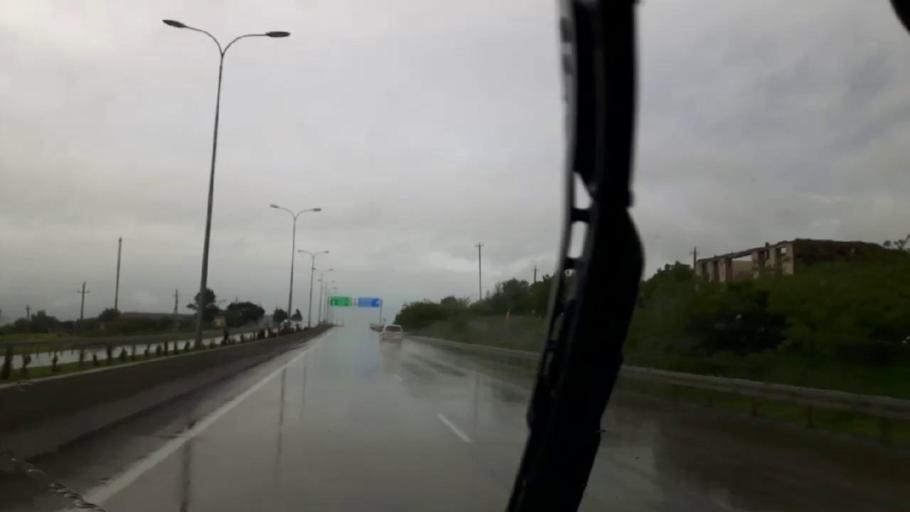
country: GE
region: Shida Kartli
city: Gori
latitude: 42.0268
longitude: 44.1967
